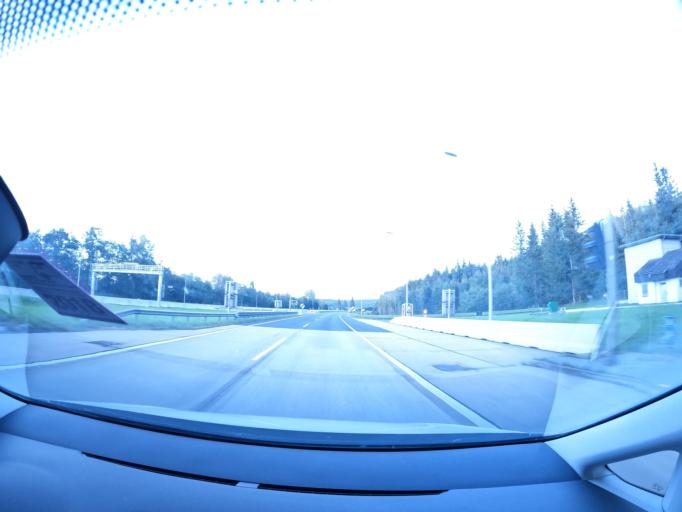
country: AT
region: Styria
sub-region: Politischer Bezirk Voitsberg
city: Pack
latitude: 46.9489
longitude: 14.9915
